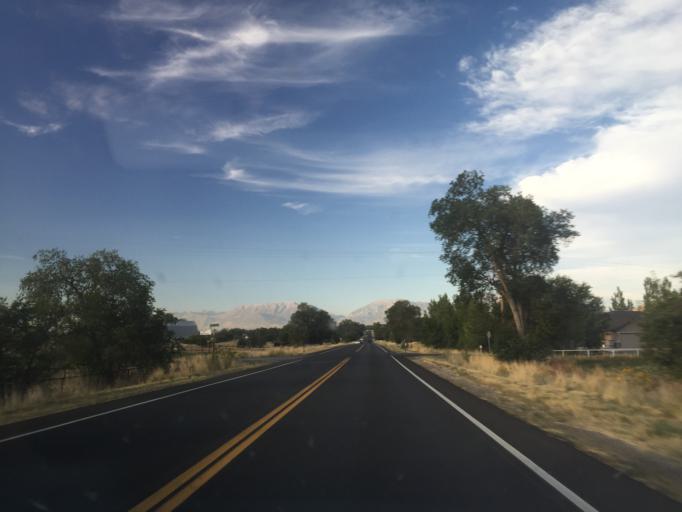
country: US
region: Utah
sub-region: Utah County
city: Santaquin
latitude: 39.9969
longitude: -111.7526
